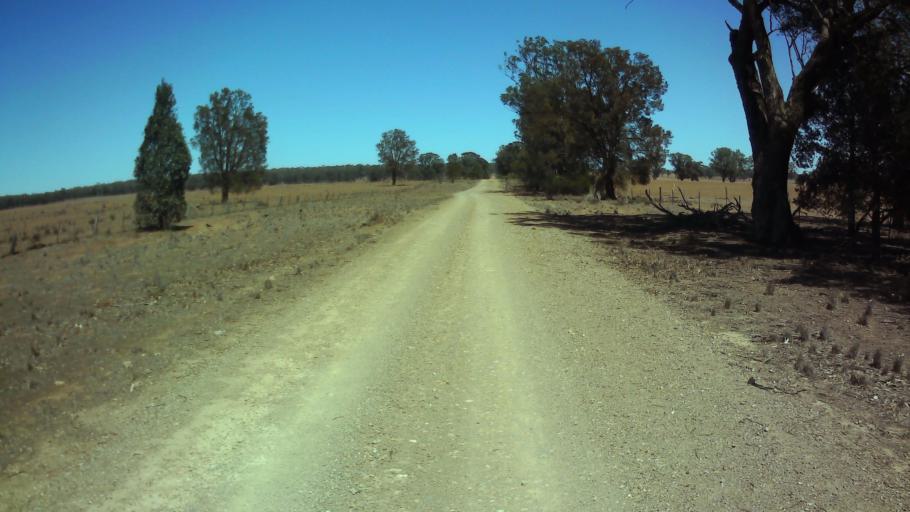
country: AU
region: New South Wales
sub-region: Forbes
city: Forbes
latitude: -33.6991
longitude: 147.8614
